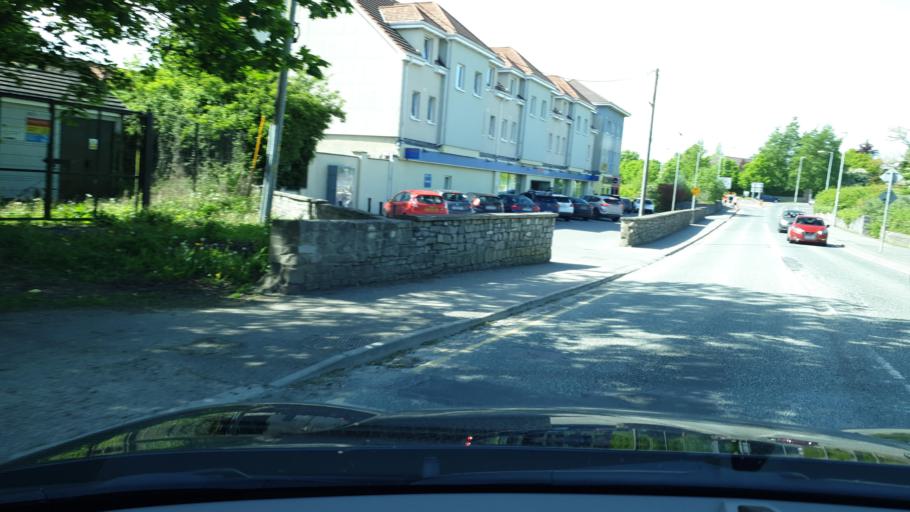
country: IE
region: Leinster
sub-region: An Mhi
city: Ratoath
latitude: 53.5044
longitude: -6.4666
